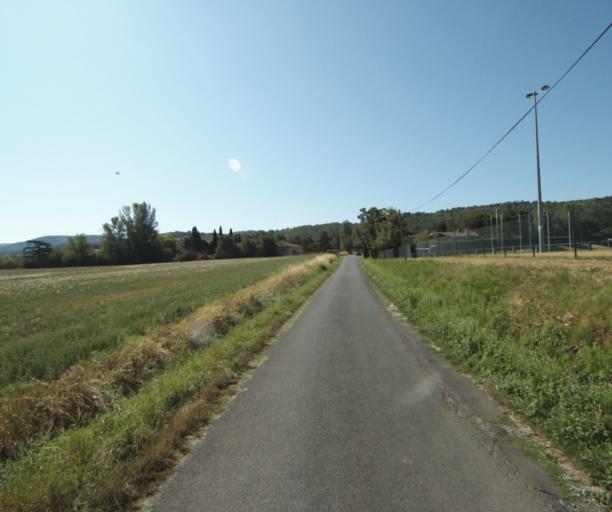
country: FR
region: Midi-Pyrenees
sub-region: Departement de la Haute-Garonne
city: Revel
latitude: 43.4528
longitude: 2.0180
